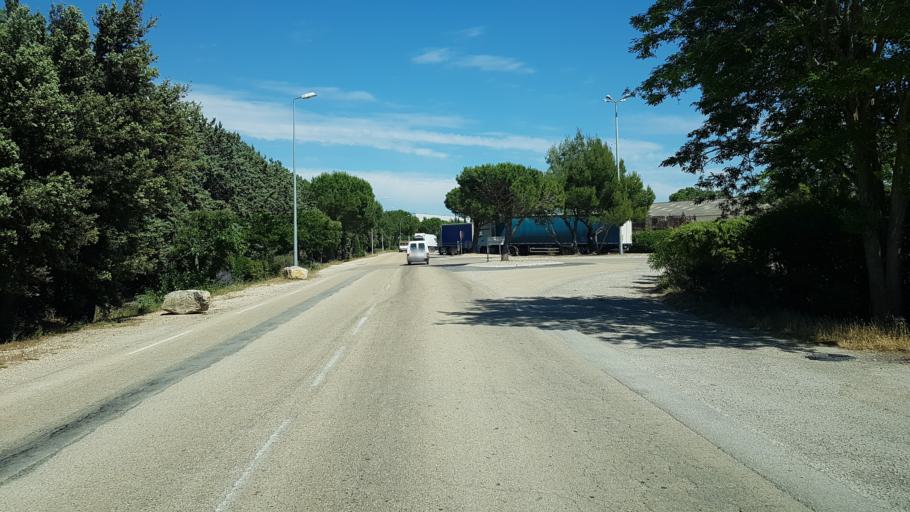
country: FR
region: Provence-Alpes-Cote d'Azur
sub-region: Departement des Bouches-du-Rhone
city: Saint-Martin-de-Crau
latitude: 43.6219
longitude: 4.7894
